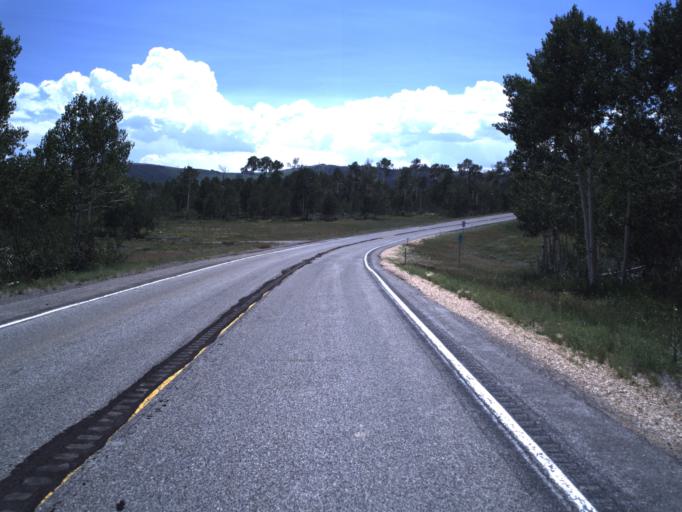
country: US
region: Utah
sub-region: Sanpete County
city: Fairview
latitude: 39.6615
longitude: -111.3287
